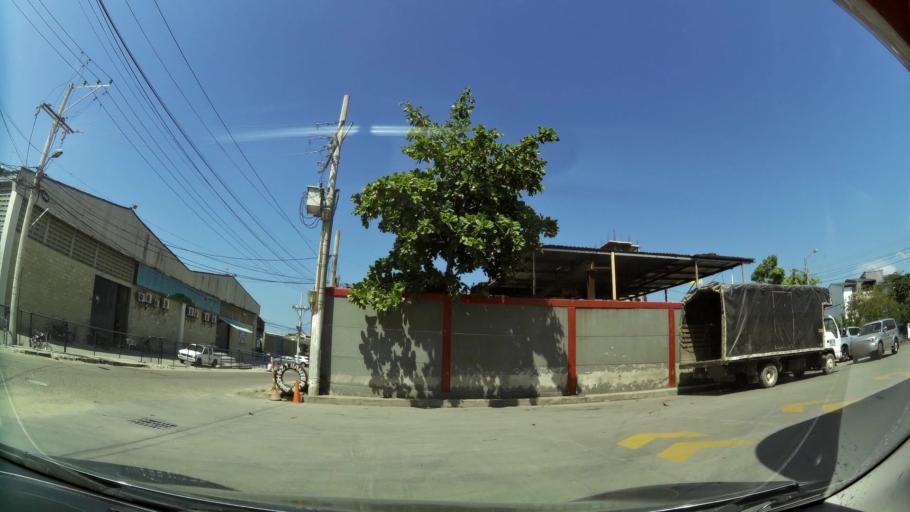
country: CO
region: Bolivar
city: Cartagena
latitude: 10.3862
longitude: -75.5019
